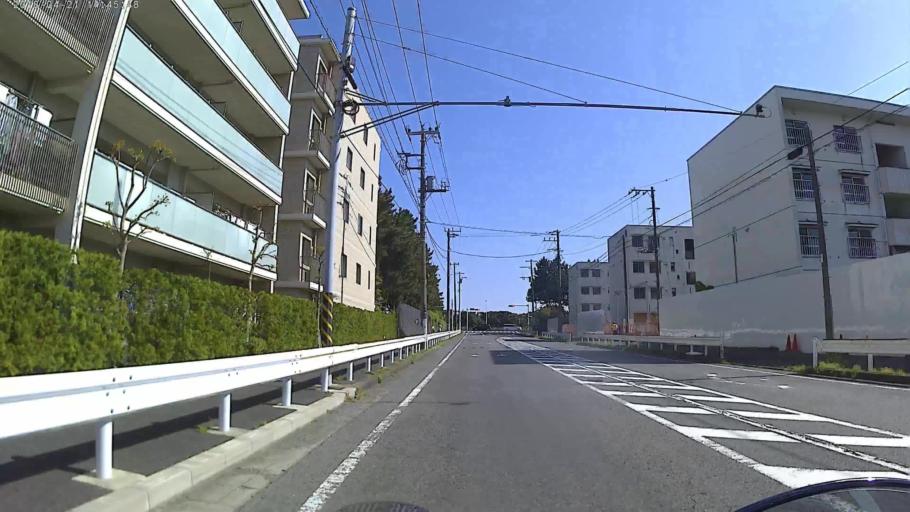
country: JP
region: Kanagawa
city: Hiratsuka
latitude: 35.3170
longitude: 139.3478
